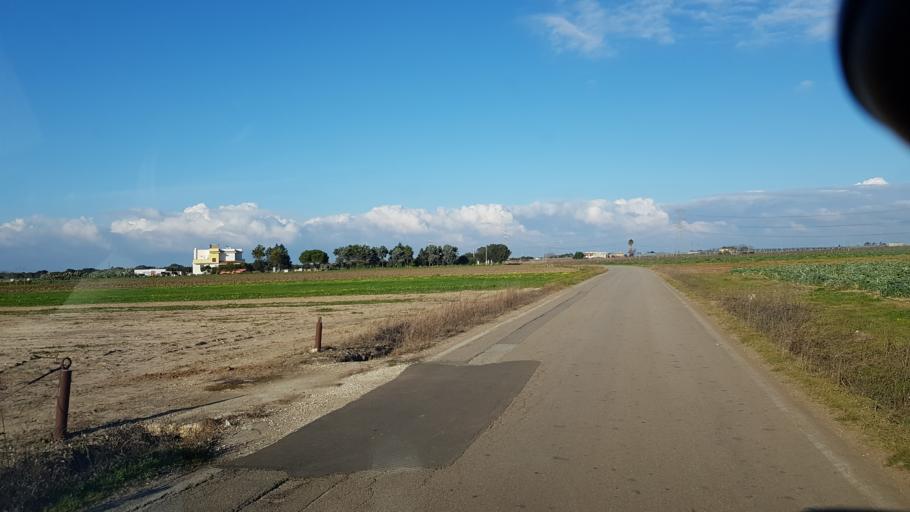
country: IT
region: Apulia
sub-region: Provincia di Brindisi
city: Tuturano
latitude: 40.5770
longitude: 17.9011
